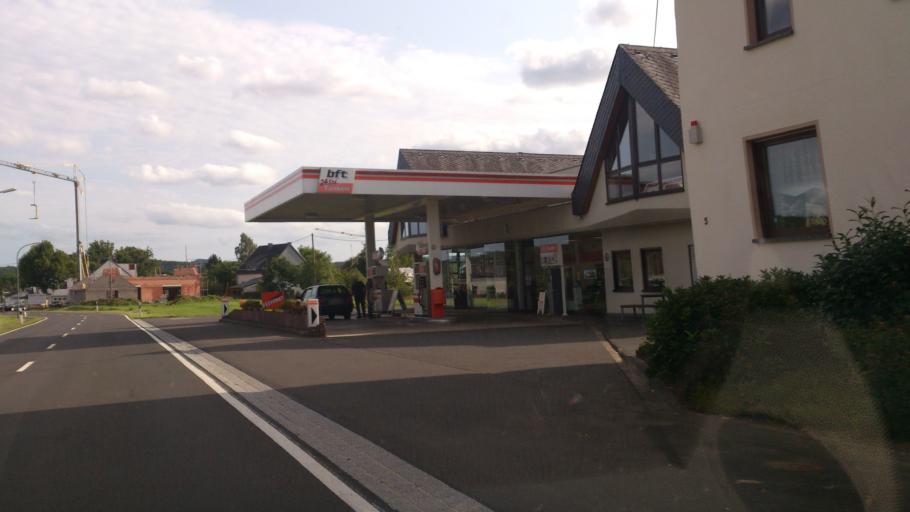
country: DE
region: Rheinland-Pfalz
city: Nohn
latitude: 50.3346
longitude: 6.7858
